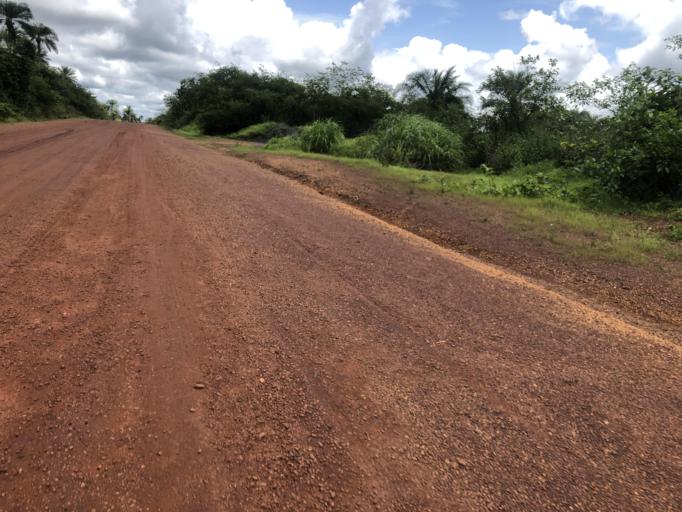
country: SL
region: Northern Province
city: Port Loko
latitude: 8.7173
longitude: -12.8416
